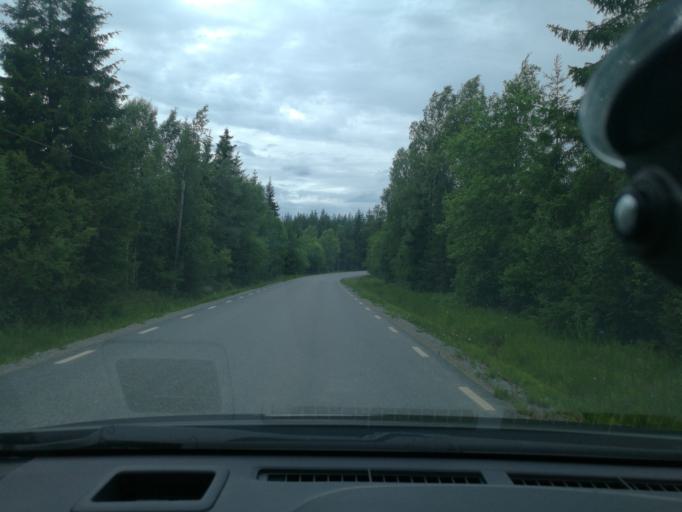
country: SE
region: Vaestmanland
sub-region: Vasteras
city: Skultuna
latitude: 59.8130
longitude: 16.3256
